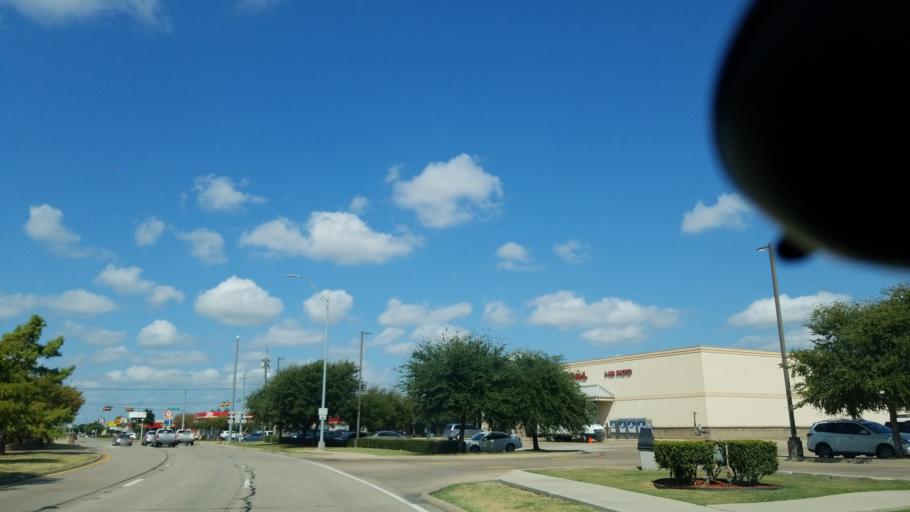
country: US
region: Texas
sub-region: Dallas County
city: Grand Prairie
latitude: 32.7094
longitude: -96.9929
